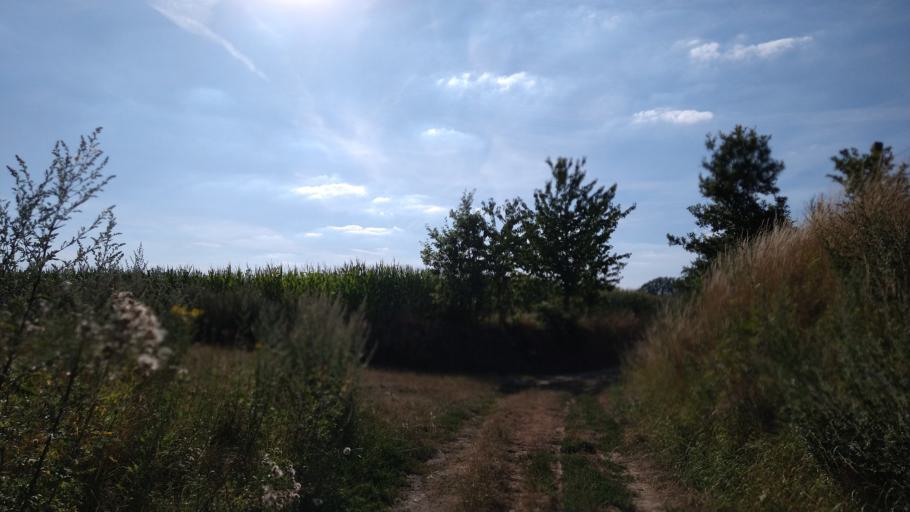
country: BE
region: Flanders
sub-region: Provincie Vlaams-Brabant
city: Huldenberg
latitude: 50.8349
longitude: 4.5780
